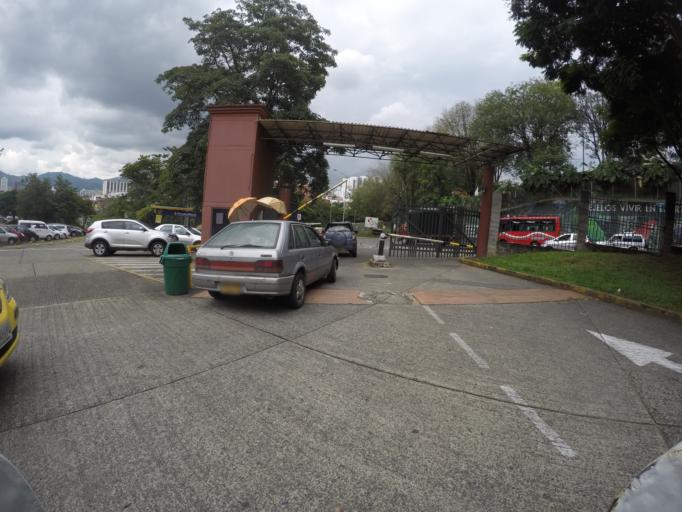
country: CO
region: Risaralda
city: Pereira
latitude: 4.8024
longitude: -75.6942
